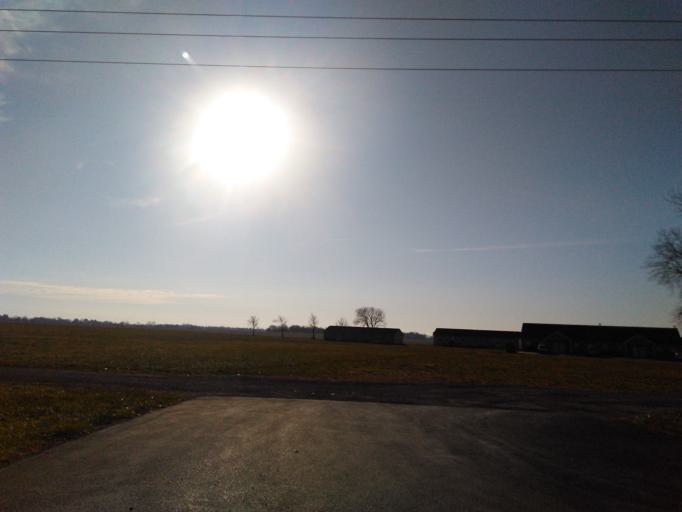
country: US
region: Illinois
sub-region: Bond County
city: Greenville
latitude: 38.8744
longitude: -89.4023
